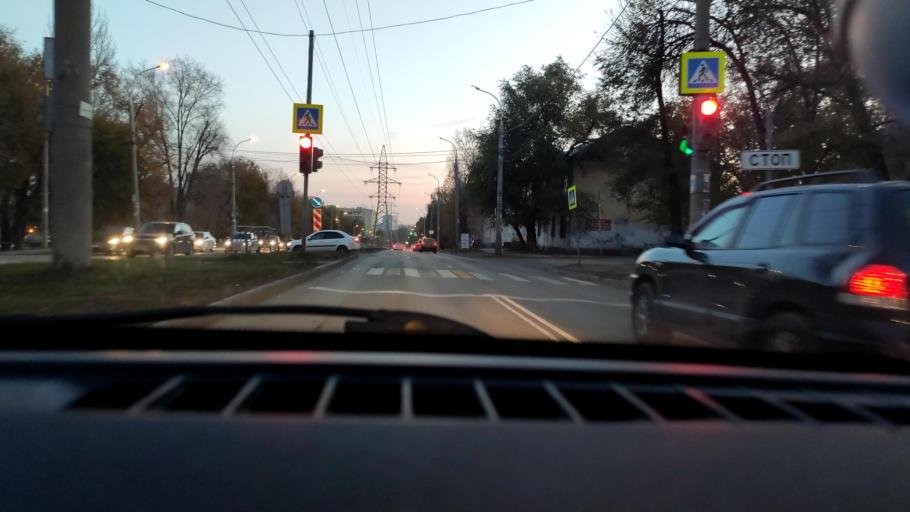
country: RU
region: Samara
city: Samara
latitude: 53.2035
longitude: 50.2137
